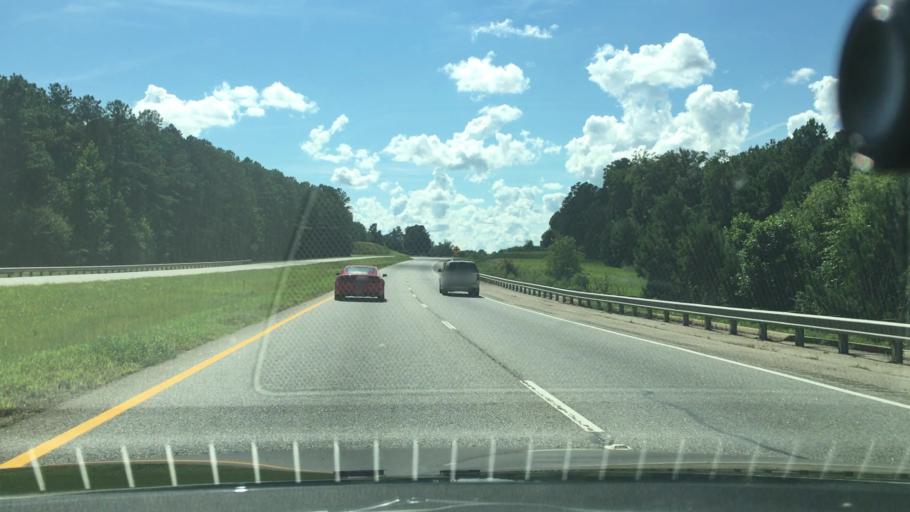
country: US
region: Georgia
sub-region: Henry County
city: Locust Grove
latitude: 33.2586
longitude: -84.1098
